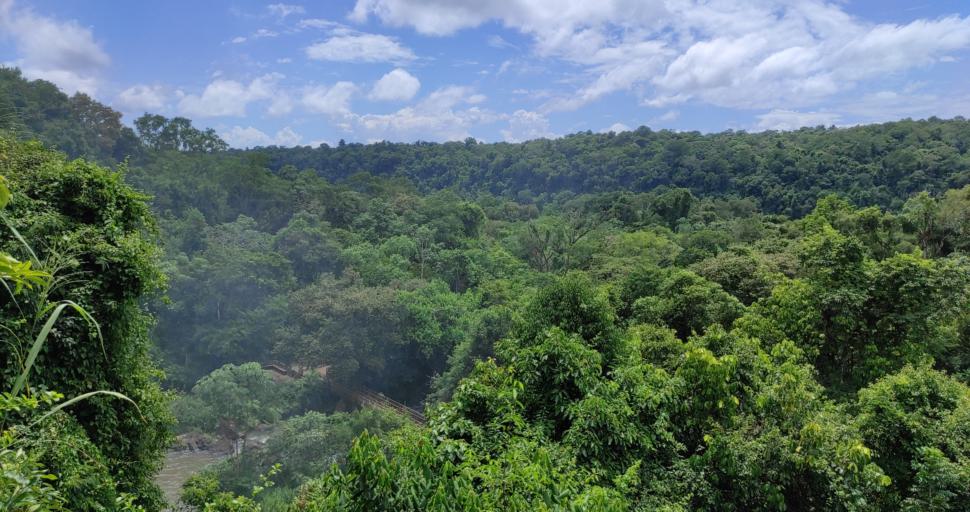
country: AR
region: Misiones
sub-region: Departamento de Iguazu
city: Puerto Iguazu
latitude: -25.6843
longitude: -54.4457
